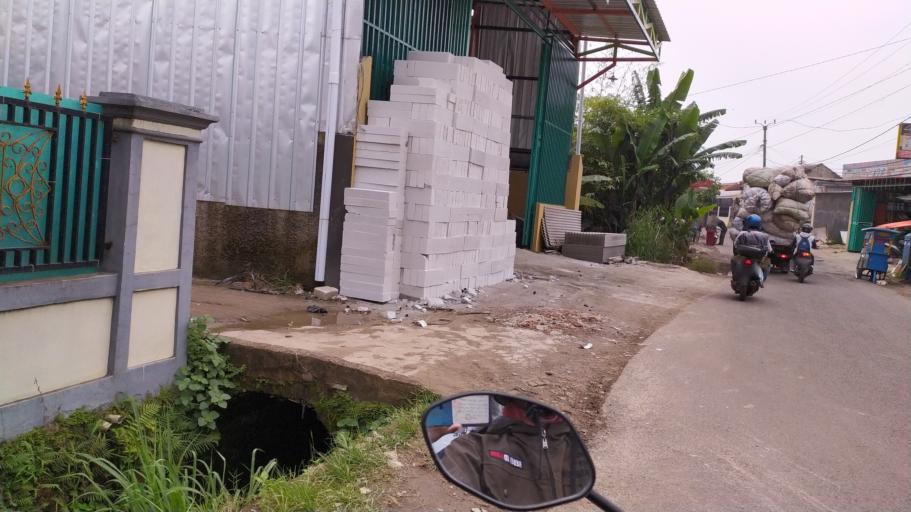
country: ID
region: West Java
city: Ciampea
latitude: -6.5877
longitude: 106.7051
